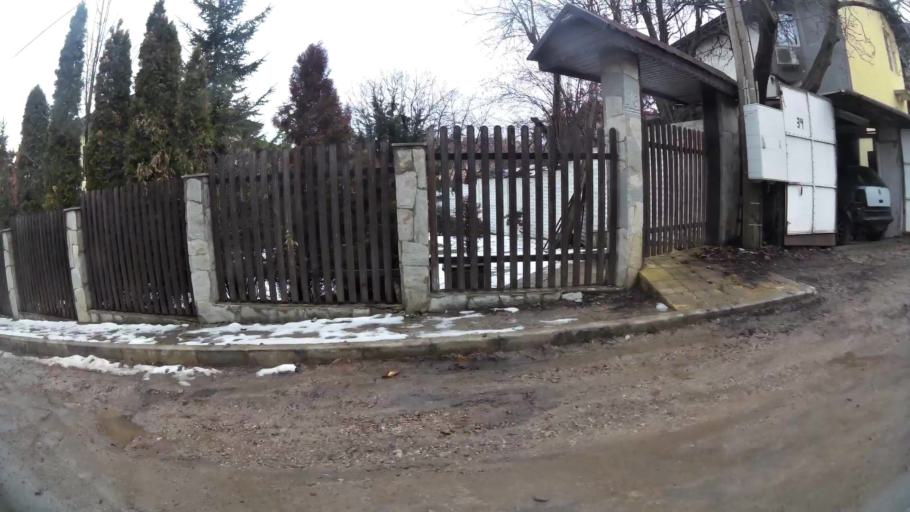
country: BG
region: Sofiya
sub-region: Obshtina Bozhurishte
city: Bozhurishte
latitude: 42.6831
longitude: 23.2339
